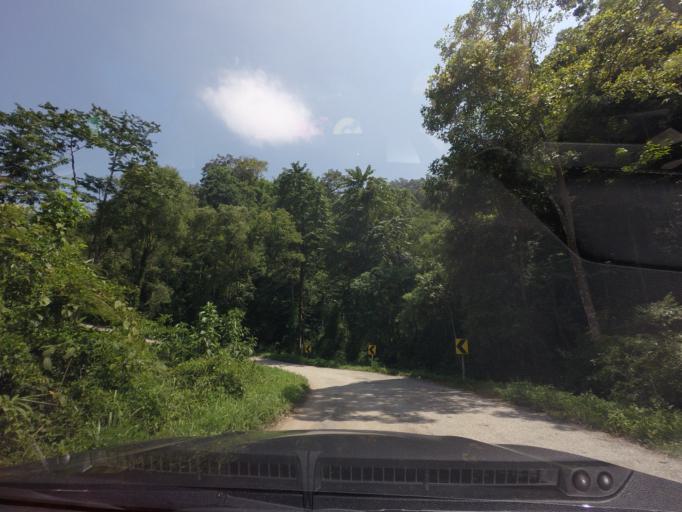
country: TH
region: Loei
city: Na Haeo
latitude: 17.6160
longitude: 100.8990
